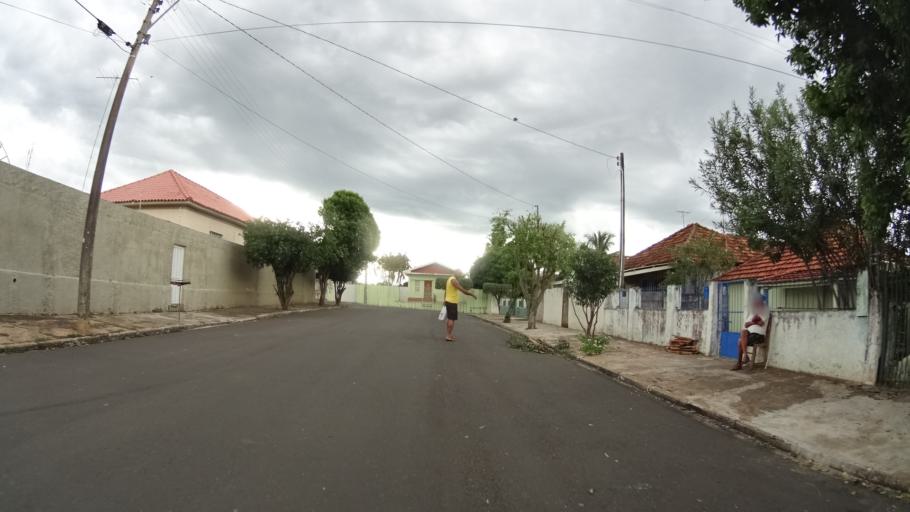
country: BR
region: Sao Paulo
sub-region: Marilia
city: Marilia
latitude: -22.2158
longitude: -49.8269
